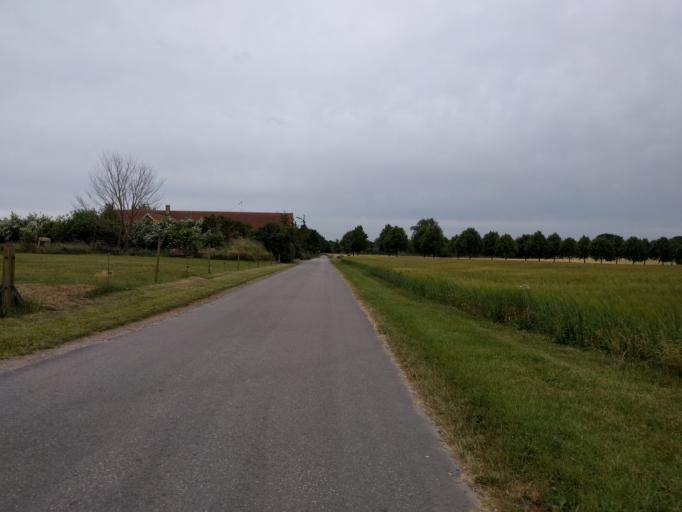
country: DK
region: South Denmark
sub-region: Kerteminde Kommune
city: Langeskov
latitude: 55.3949
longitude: 10.5933
